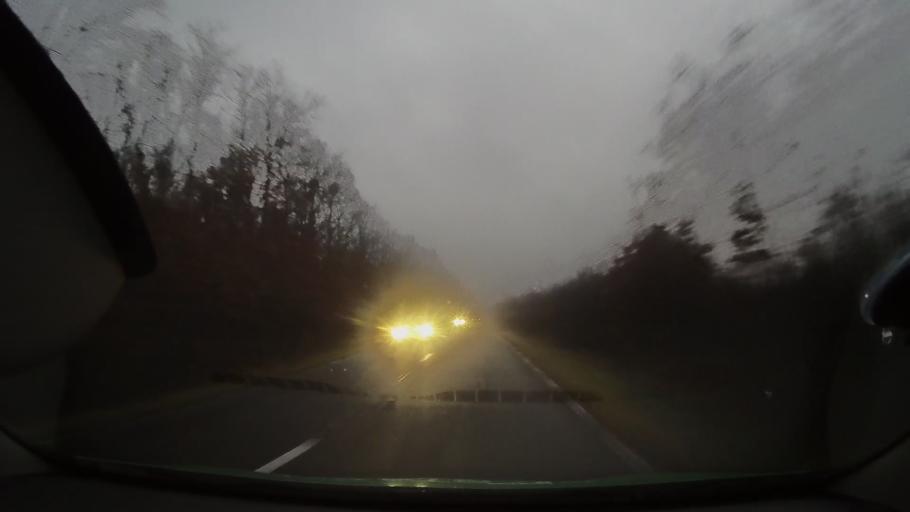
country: RO
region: Arad
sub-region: Comuna Craiova
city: Craiova
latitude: 46.5302
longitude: 21.9548
